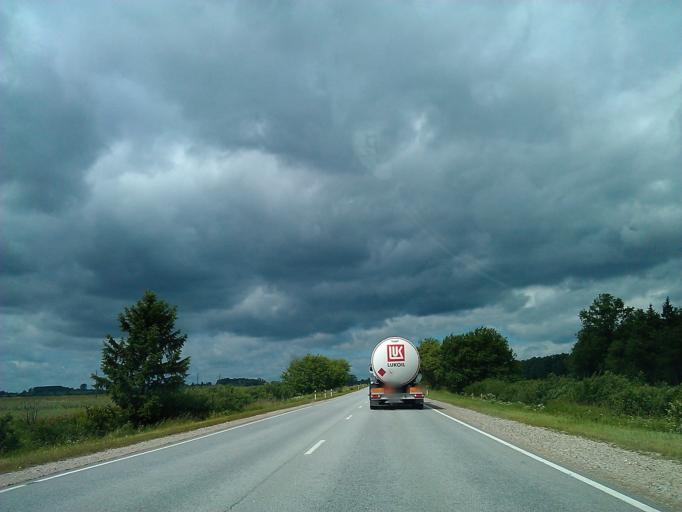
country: LV
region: Engure
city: Smarde
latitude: 56.9203
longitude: 23.2999
